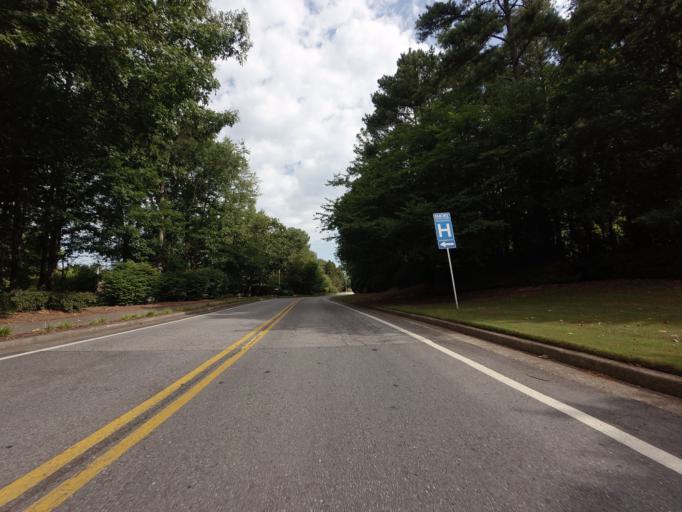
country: US
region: Georgia
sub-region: Gwinnett County
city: Duluth
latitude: 34.0535
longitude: -84.1438
